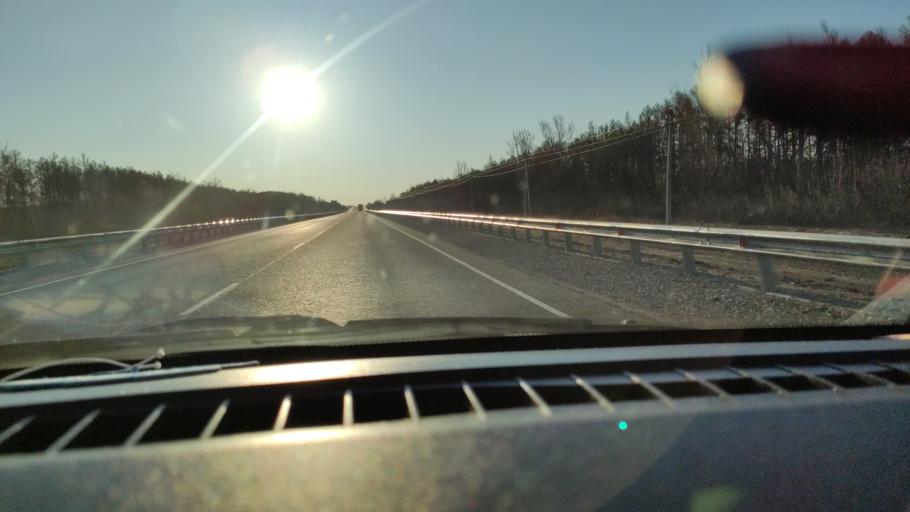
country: RU
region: Saratov
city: Shikhany
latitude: 52.1612
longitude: 47.1453
